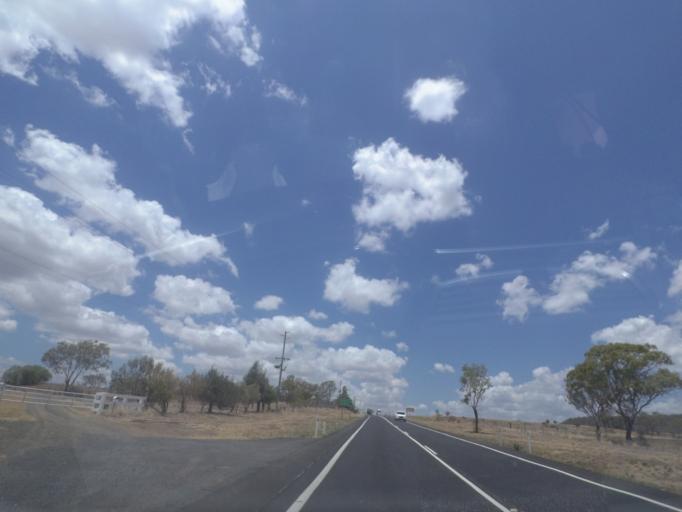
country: AU
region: Queensland
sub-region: Toowoomba
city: Top Camp
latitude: -27.7284
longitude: 151.9119
